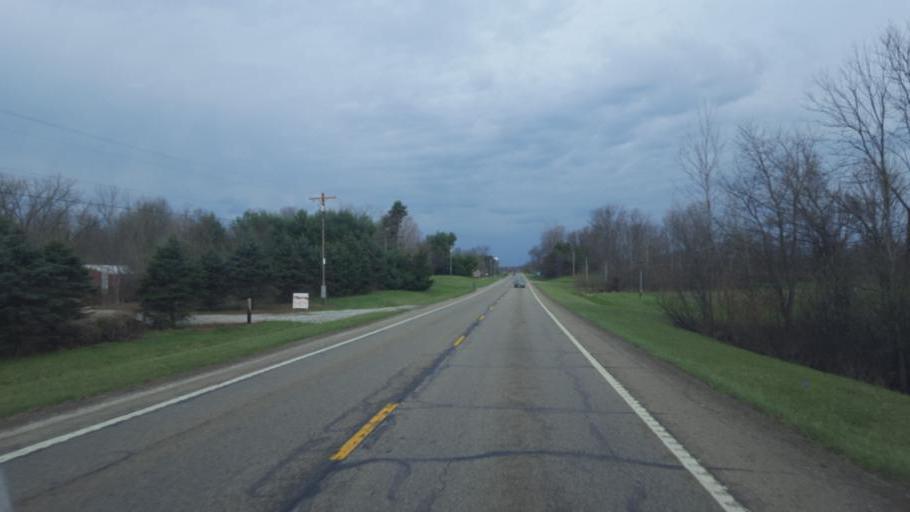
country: US
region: Ohio
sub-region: Morrow County
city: Mount Gilead
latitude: 40.5207
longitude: -82.7506
